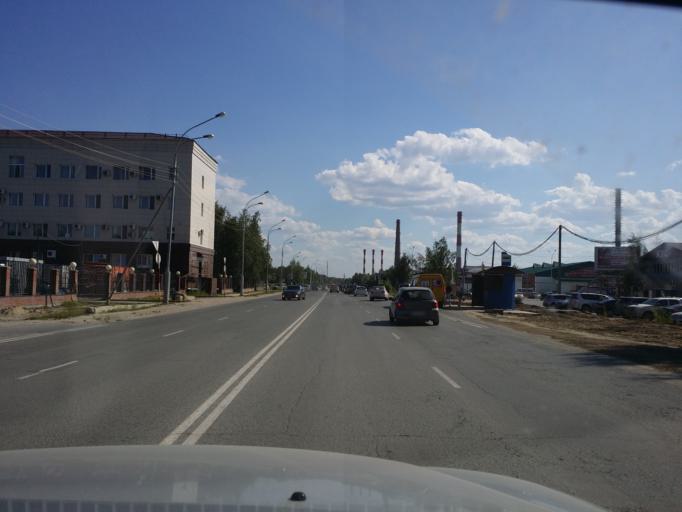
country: RU
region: Khanty-Mansiyskiy Avtonomnyy Okrug
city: Nizhnevartovsk
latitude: 60.9408
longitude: 76.5485
